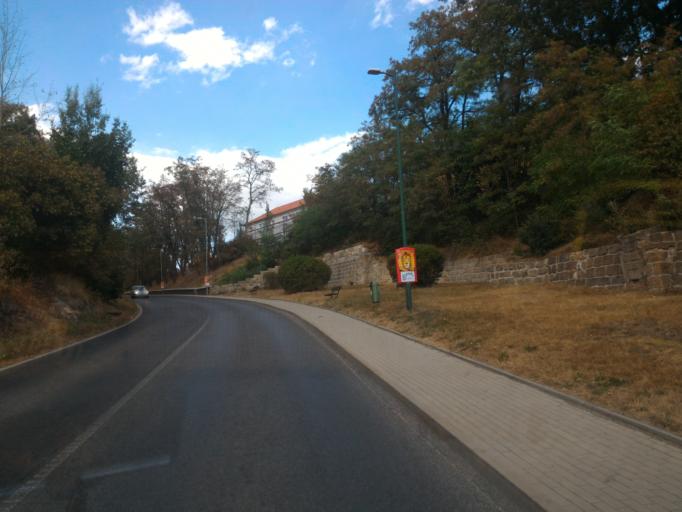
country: CZ
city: Mimon
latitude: 50.6626
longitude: 14.7249
